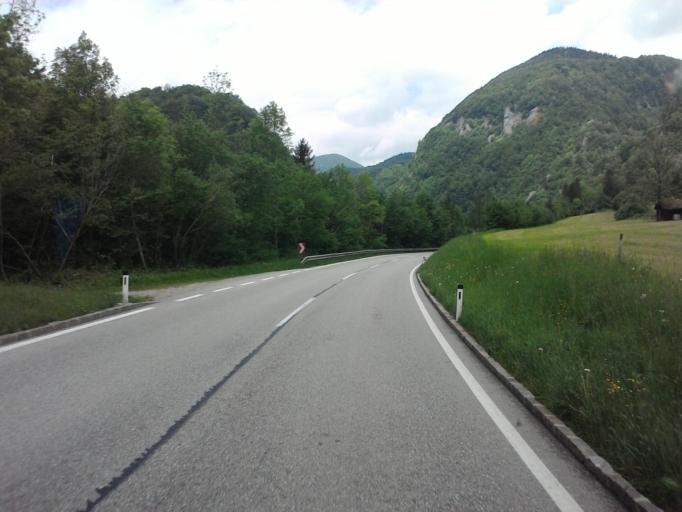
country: AT
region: Upper Austria
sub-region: Politischer Bezirk Steyr-Land
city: Weyer
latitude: 47.8643
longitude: 14.6099
